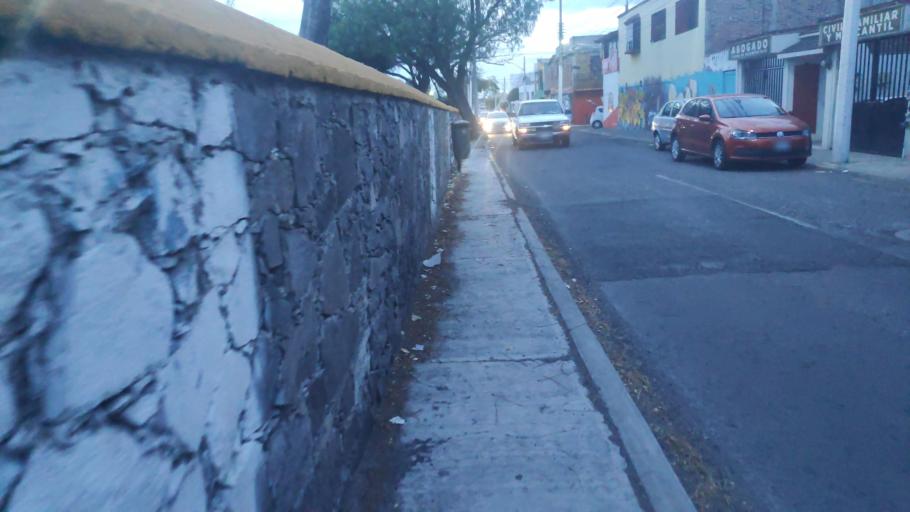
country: MX
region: Queretaro
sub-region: Queretaro
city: Santiago de Queretaro
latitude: 20.5797
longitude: -100.3799
